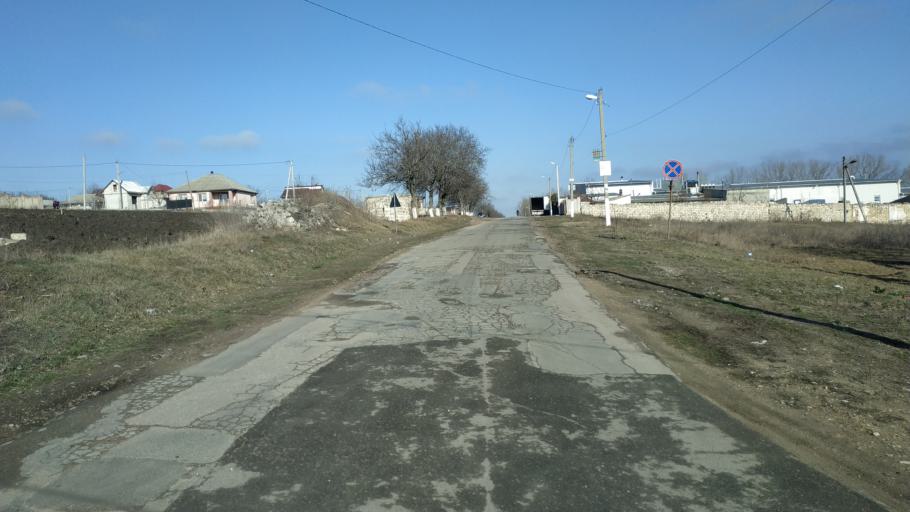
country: MD
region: Laloveni
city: Ialoveni
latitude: 46.9442
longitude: 28.7228
